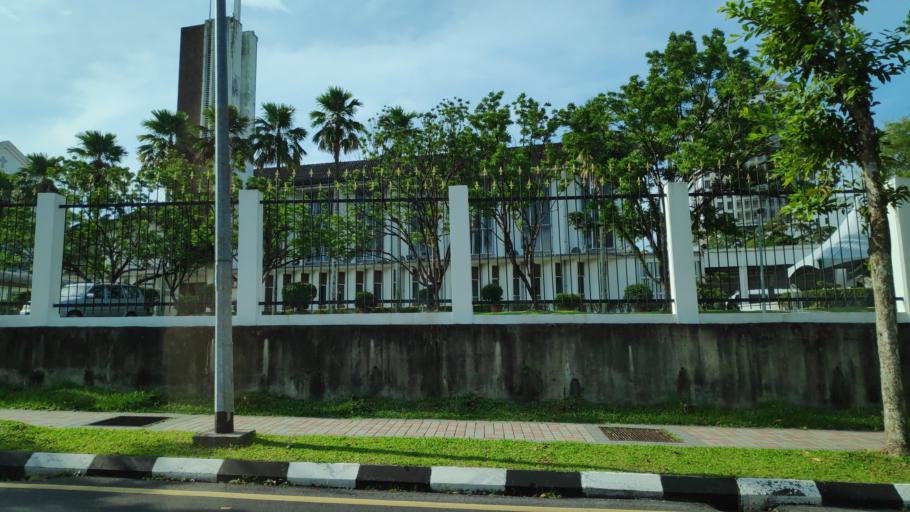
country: MY
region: Sarawak
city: Kuching
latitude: 1.5575
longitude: 110.3451
